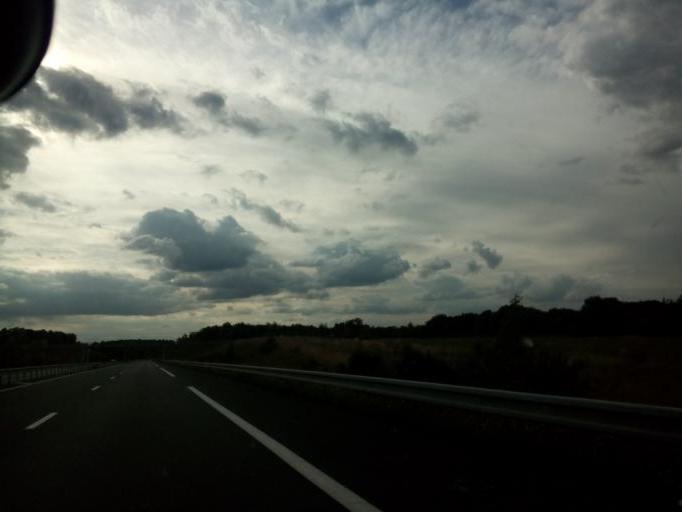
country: FR
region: Centre
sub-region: Departement du Loir-et-Cher
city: Thesee
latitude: 47.2949
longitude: 1.2523
